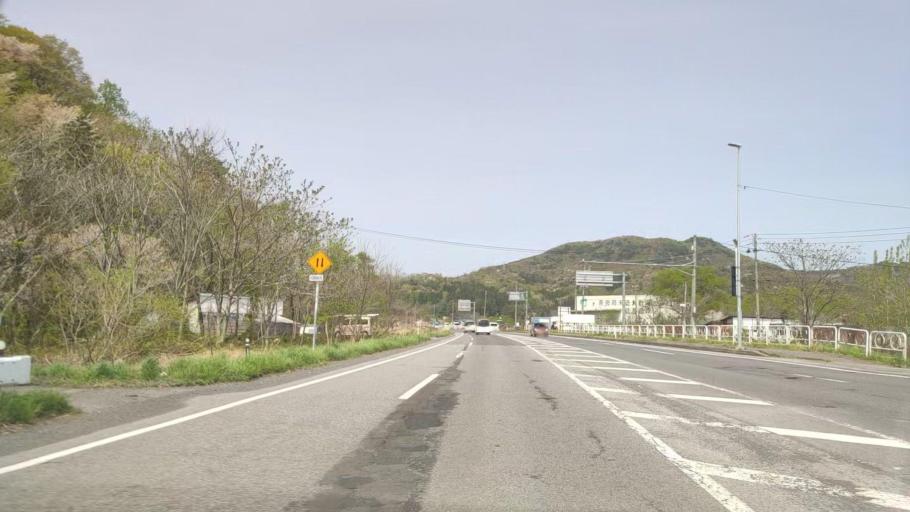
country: JP
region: Aomori
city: Aomori Shi
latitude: 40.8472
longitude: 140.8363
